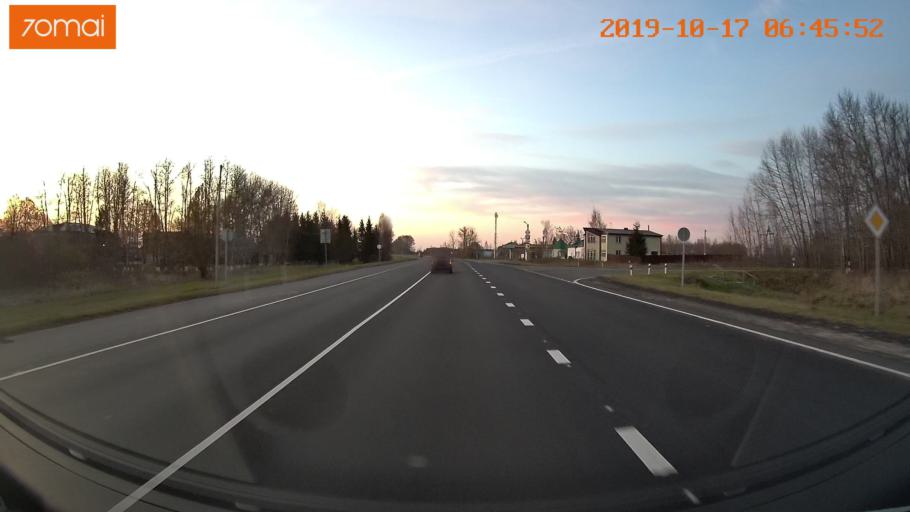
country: RU
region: Vladimir
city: Kideksha
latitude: 56.5551
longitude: 40.5479
